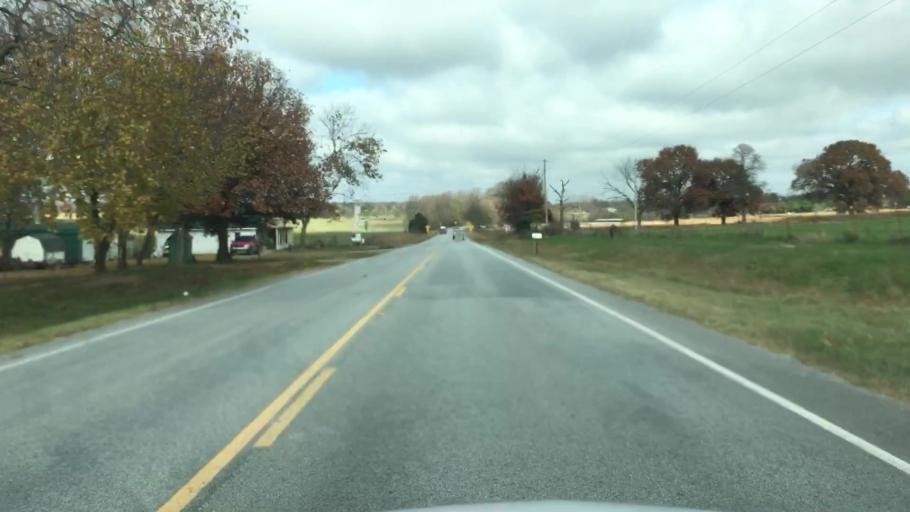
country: US
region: Arkansas
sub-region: Benton County
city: Centerton
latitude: 36.2824
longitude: -94.3501
